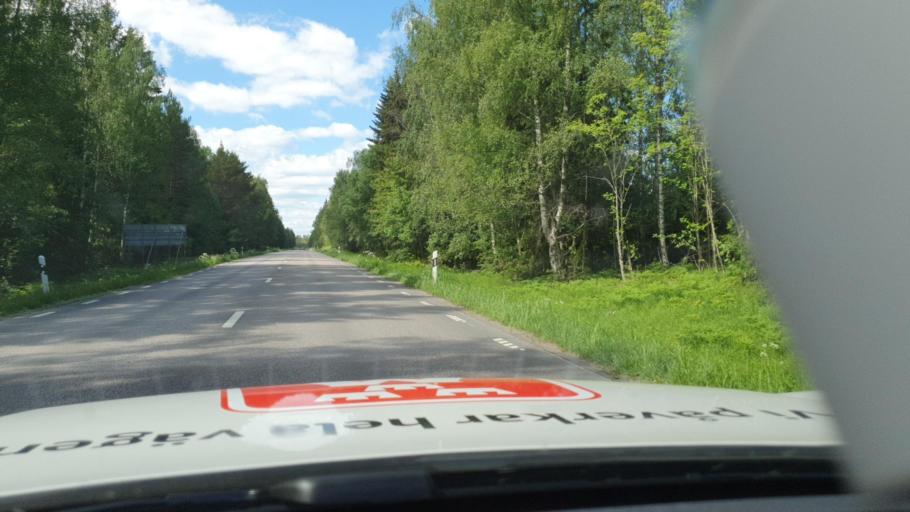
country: SE
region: Uppsala
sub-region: Tierps Kommun
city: Karlholmsbruk
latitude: 60.5251
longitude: 17.5996
